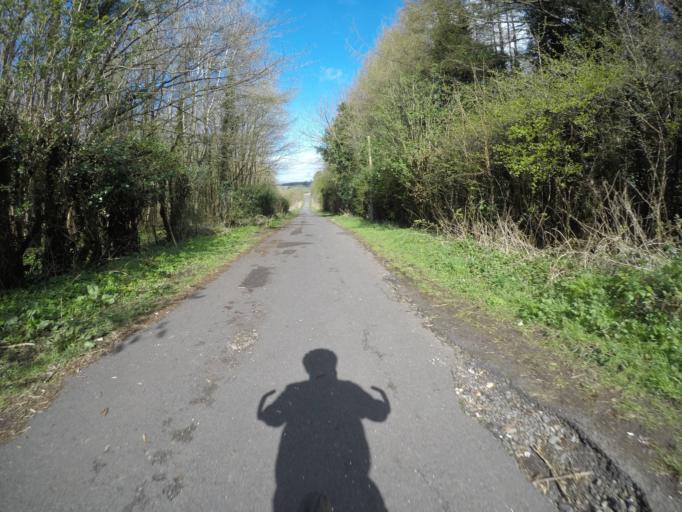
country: GB
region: Scotland
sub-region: North Ayrshire
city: Springside
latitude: 55.6128
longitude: -4.6064
